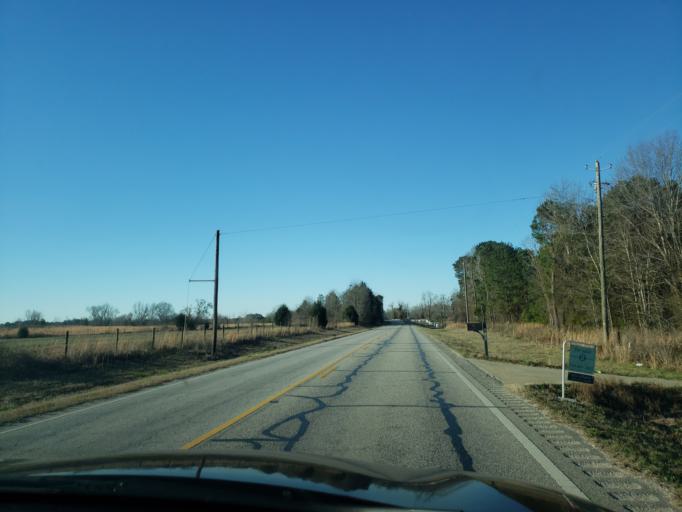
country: US
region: Alabama
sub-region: Macon County
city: Tuskegee
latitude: 32.5837
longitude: -85.6510
